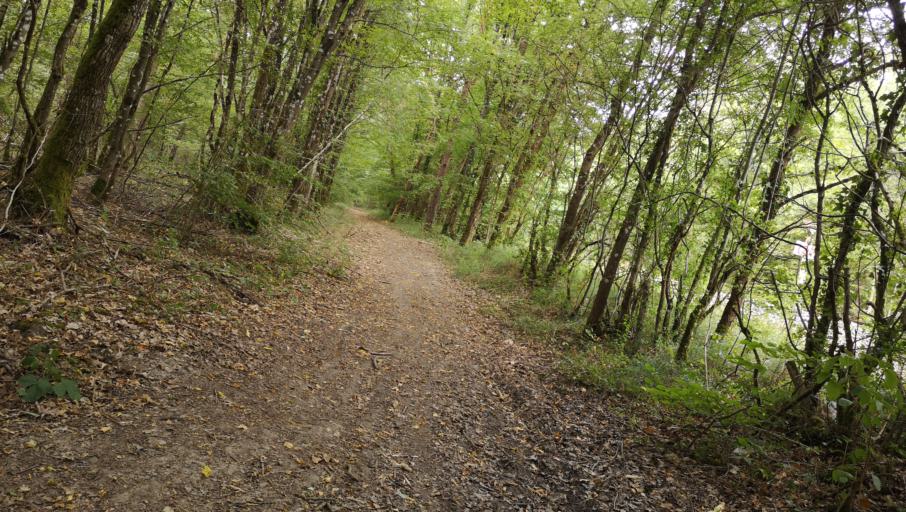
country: FR
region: Centre
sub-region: Departement du Loiret
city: Marigny-les-Usages
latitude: 47.9651
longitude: 2.0099
